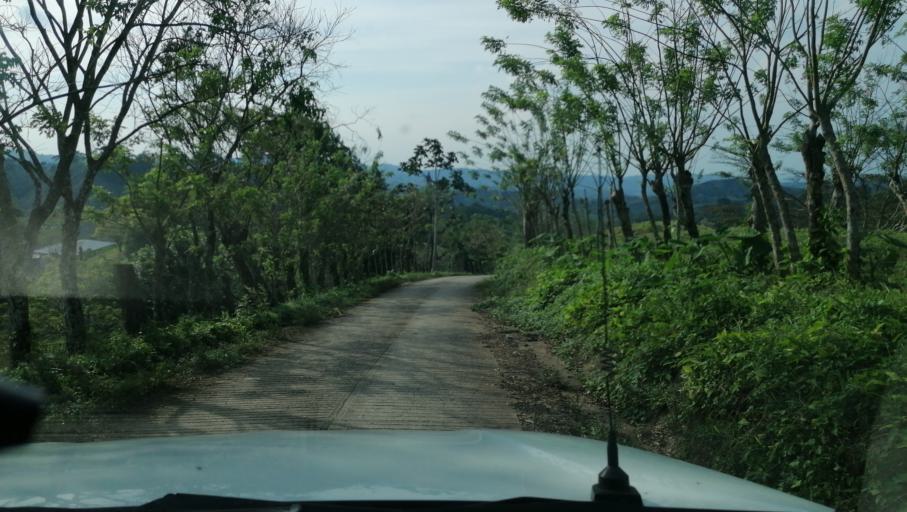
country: MX
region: Chiapas
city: Pichucalco
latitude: 17.4829
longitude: -93.2277
